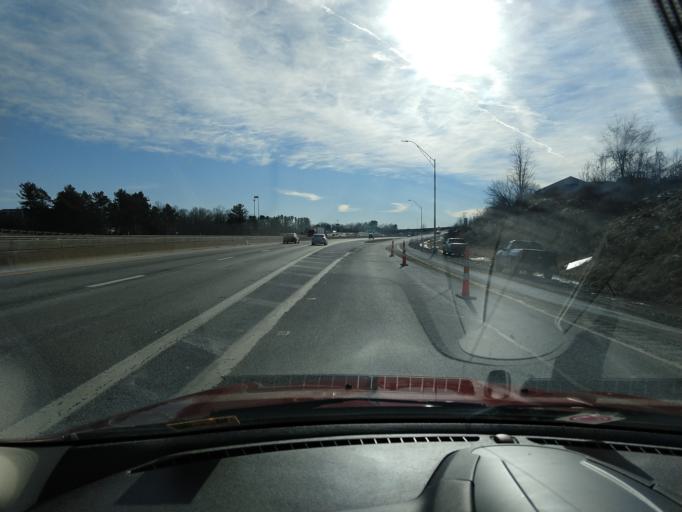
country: US
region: West Virginia
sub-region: Raleigh County
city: Mabscott
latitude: 37.7976
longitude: -81.2143
